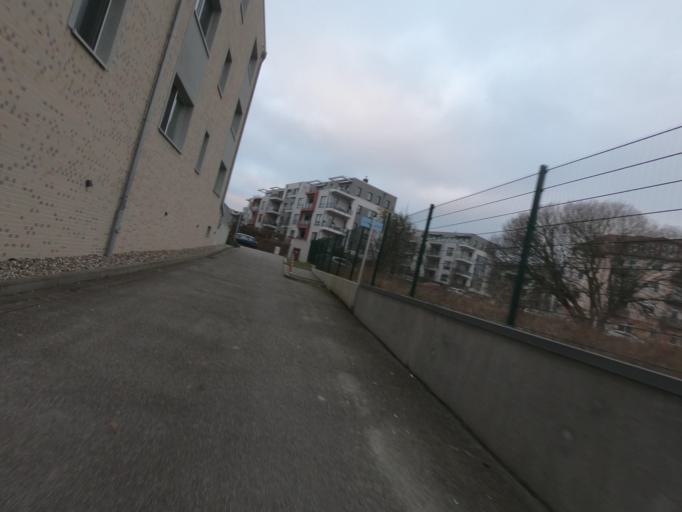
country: DE
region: Mecklenburg-Vorpommern
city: Rostock
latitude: 54.0840
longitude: 12.1467
